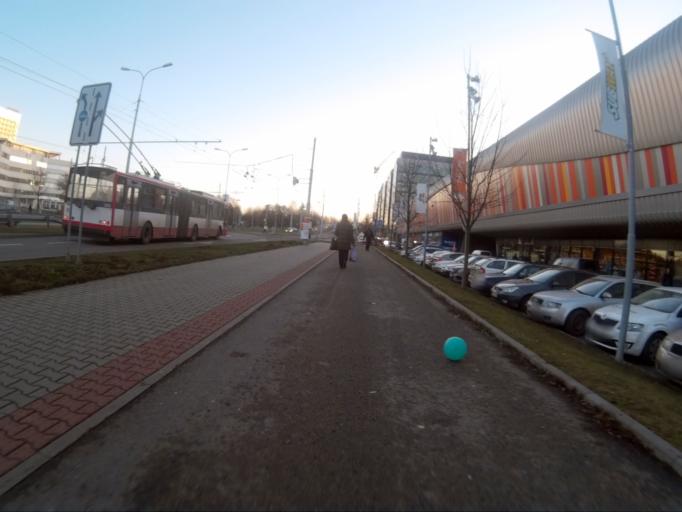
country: CZ
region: South Moravian
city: Ostopovice
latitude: 49.1771
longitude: 16.5671
